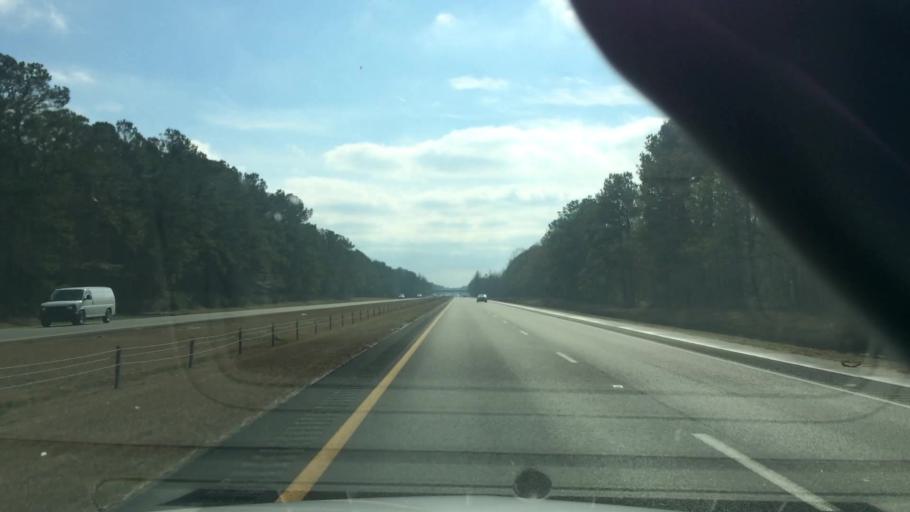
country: US
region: North Carolina
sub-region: Pender County
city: Rocky Point
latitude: 34.4911
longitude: -77.8777
